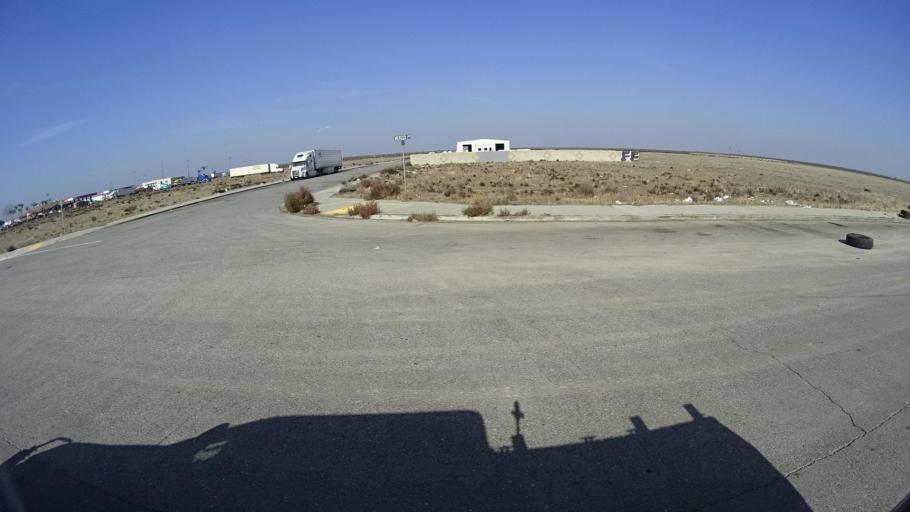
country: US
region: California
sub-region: Kern County
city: Shafter
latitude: 35.5297
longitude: -119.1851
